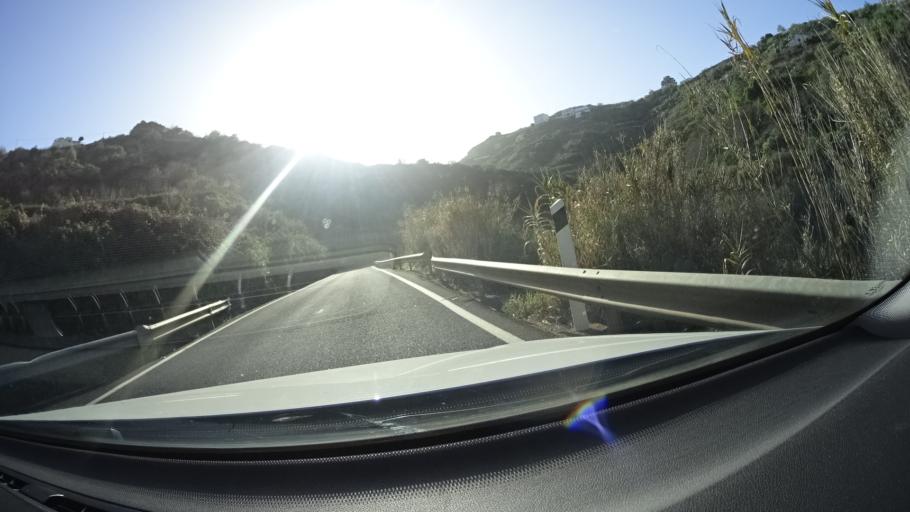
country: ES
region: Canary Islands
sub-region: Provincia de Las Palmas
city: Valleseco
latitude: 28.0251
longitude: -15.5558
